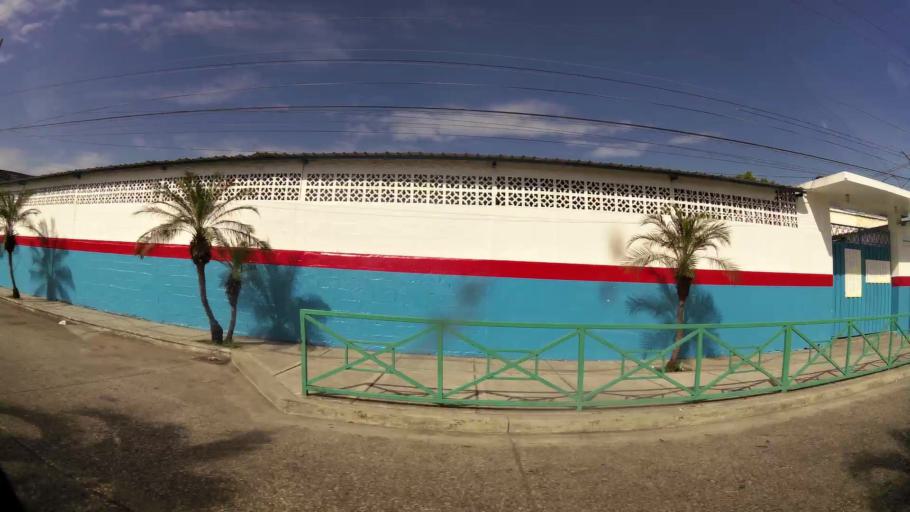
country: EC
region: Guayas
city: Guayaquil
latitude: -2.2123
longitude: -79.9124
